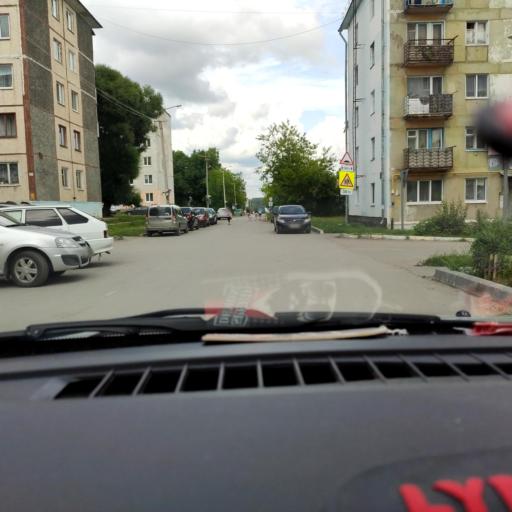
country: RU
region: Perm
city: Zvezdnyy
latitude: 57.7378
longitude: 56.3136
